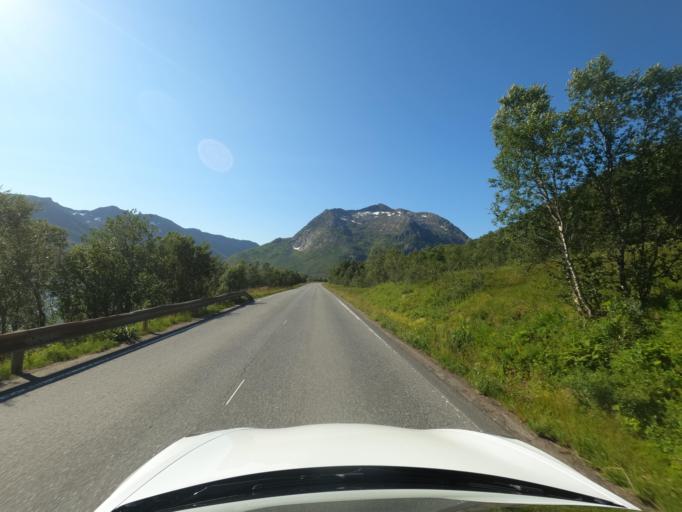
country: NO
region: Nordland
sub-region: Lodingen
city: Lodingen
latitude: 68.5487
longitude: 15.7453
